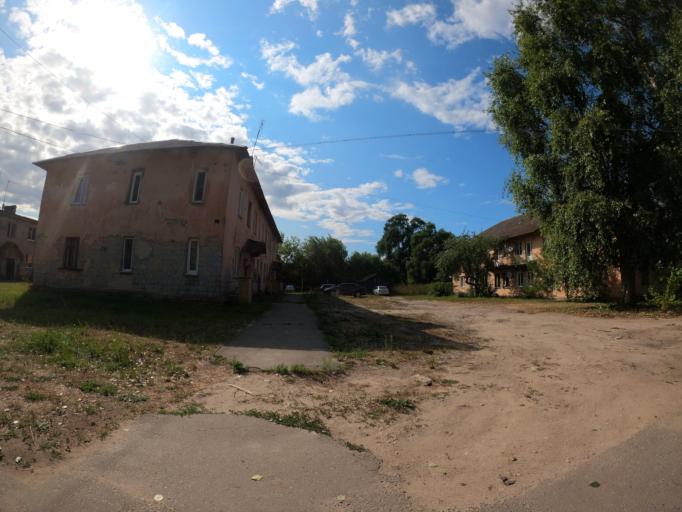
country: RU
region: Moskovskaya
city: Konobeyevo
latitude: 55.3928
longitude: 38.7086
